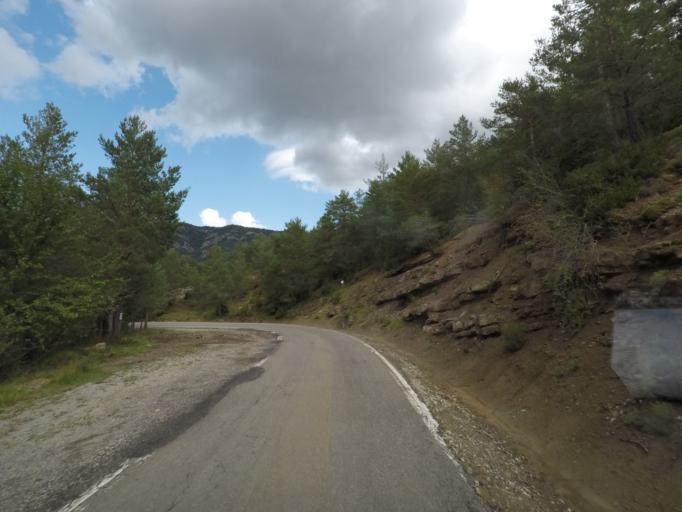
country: ES
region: Aragon
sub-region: Provincia de Huesca
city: Fiscal
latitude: 42.4079
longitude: -0.1482
